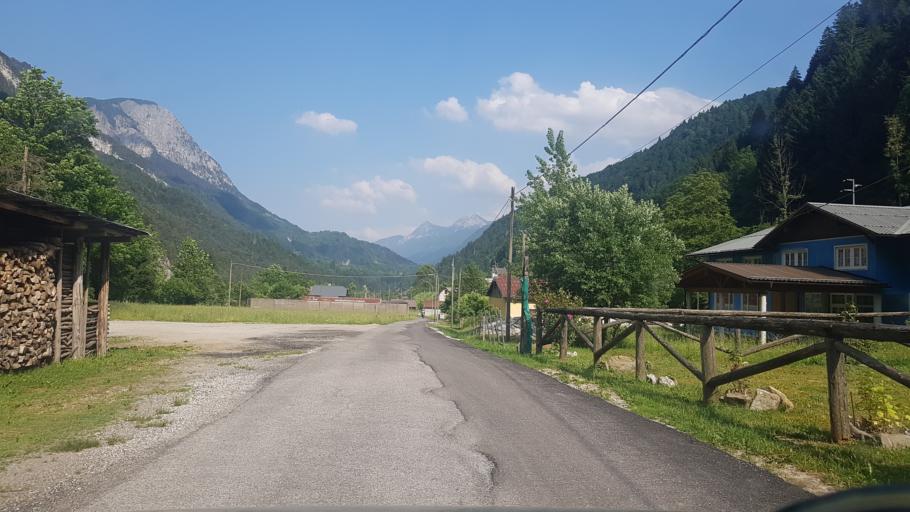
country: IT
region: Friuli Venezia Giulia
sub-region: Provincia di Udine
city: Pontebba
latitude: 46.5225
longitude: 13.2656
